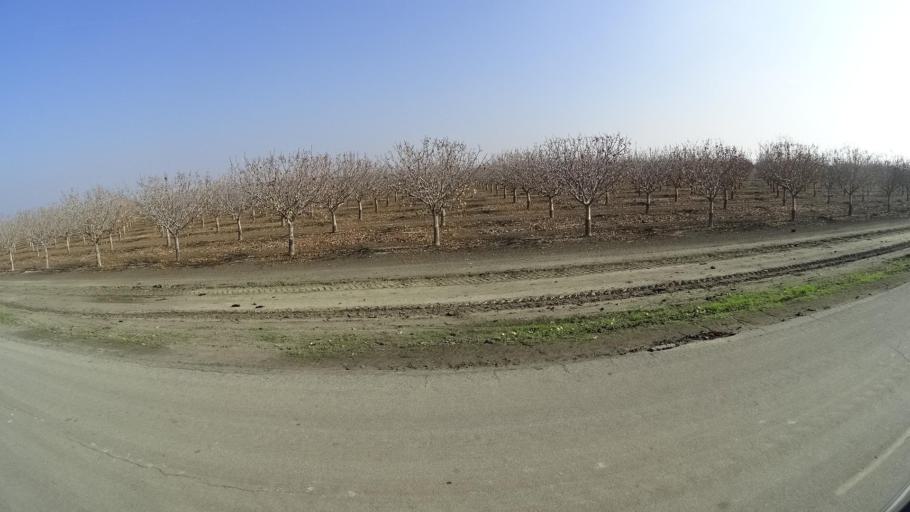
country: US
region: California
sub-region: Kern County
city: Buttonwillow
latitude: 35.3531
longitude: -119.4293
